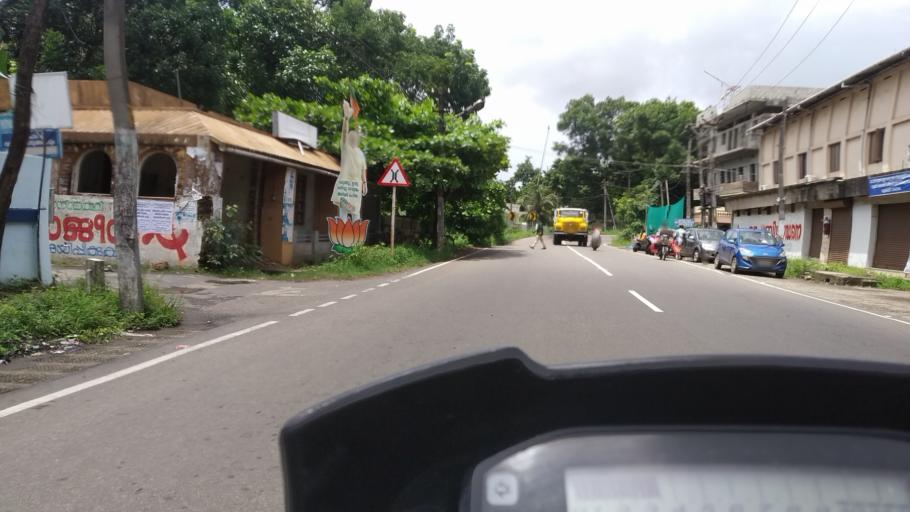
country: IN
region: Kerala
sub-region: Ernakulam
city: Aluva
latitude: 10.1304
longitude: 76.2927
